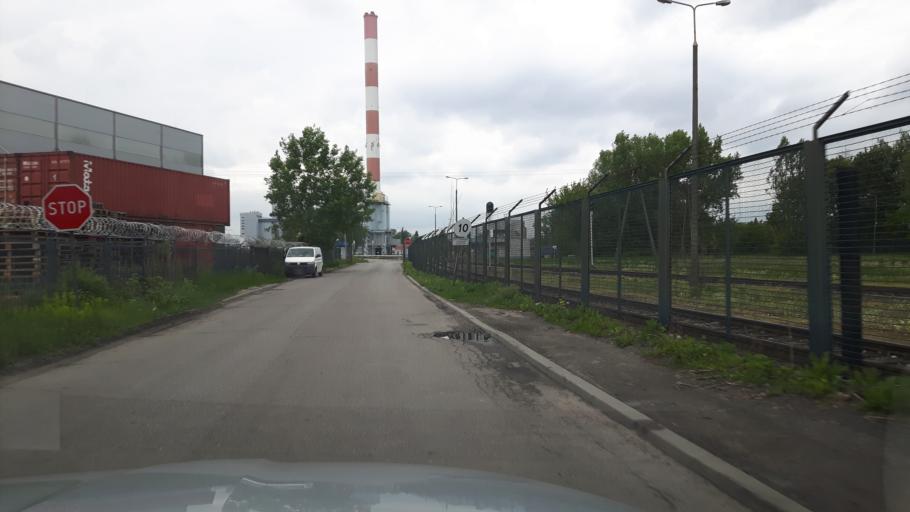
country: PL
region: Masovian Voivodeship
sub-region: Warszawa
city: Rembertow
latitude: 52.2607
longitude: 21.1351
